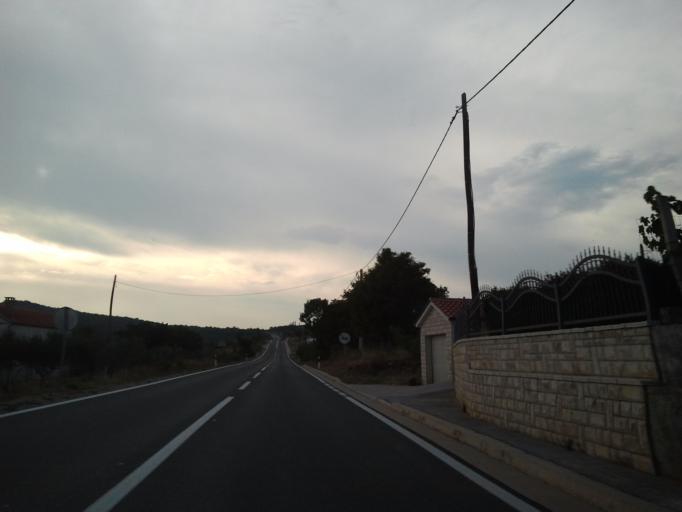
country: HR
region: Zadarska
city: Posedarje
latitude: 44.2214
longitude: 15.4486
